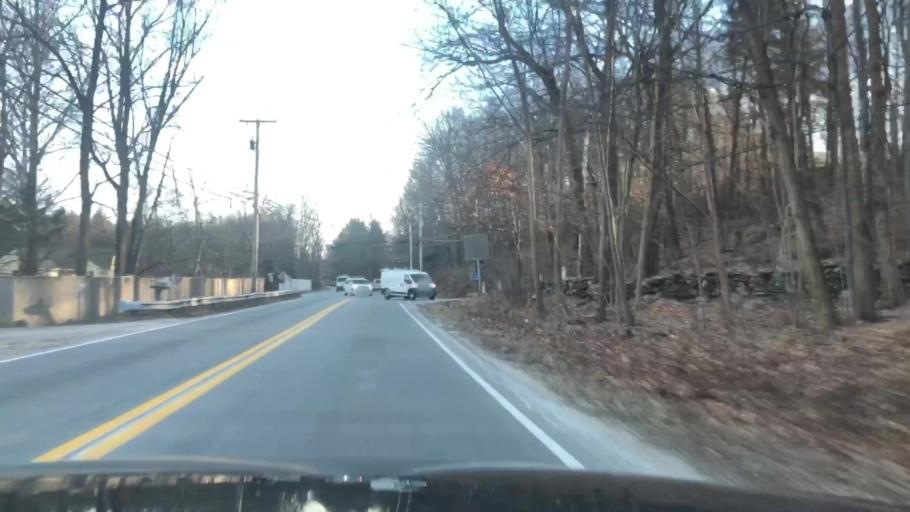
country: US
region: Massachusetts
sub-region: Worcester County
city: Bolton
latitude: 42.4412
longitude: -71.6204
